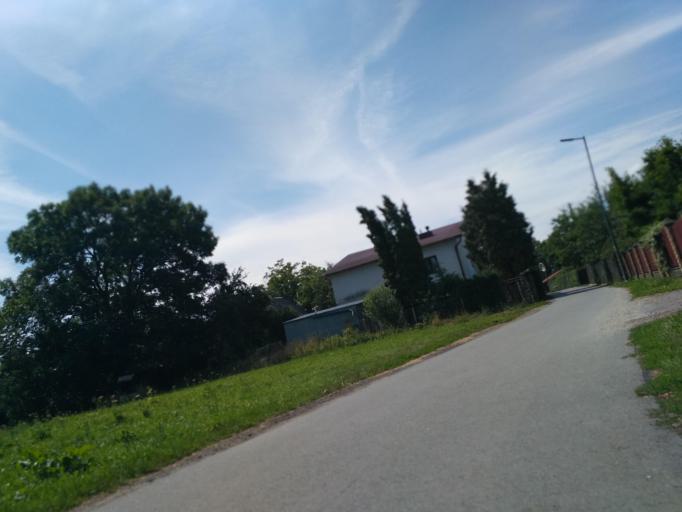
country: PL
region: Subcarpathian Voivodeship
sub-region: Powiat krosnienski
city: Kroscienko Wyzne
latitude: 49.6802
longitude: 21.8613
